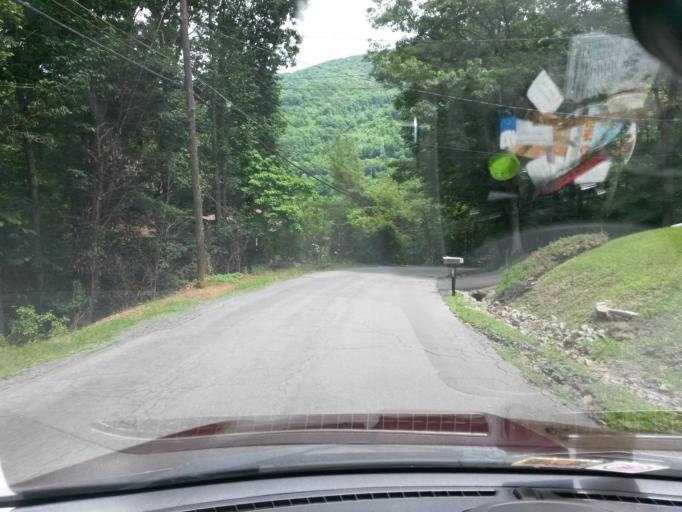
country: US
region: Virginia
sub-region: City of Covington
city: Fairlawn
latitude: 37.7820
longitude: -79.9190
